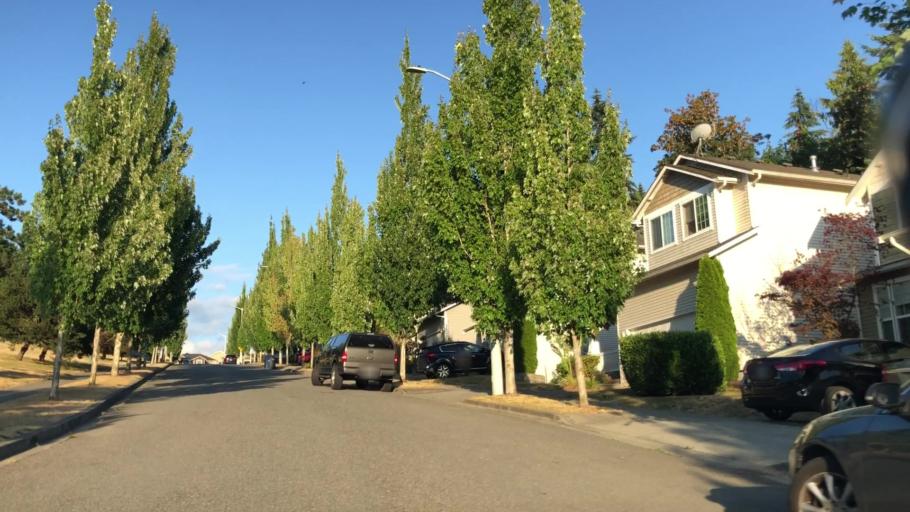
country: US
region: Washington
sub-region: Snohomish County
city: Martha Lake
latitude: 47.8611
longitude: -122.2626
